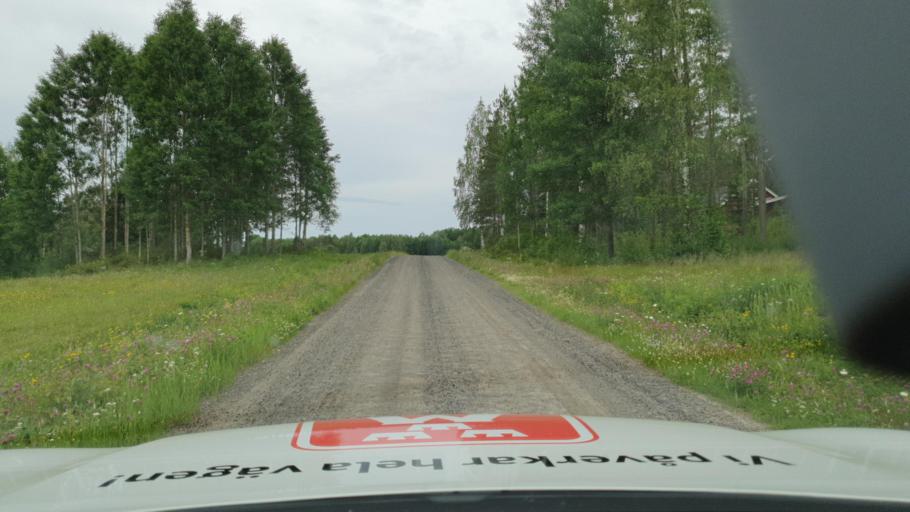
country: SE
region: Vaesterbotten
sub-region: Robertsfors Kommun
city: Robertsfors
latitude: 64.2020
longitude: 20.7021
